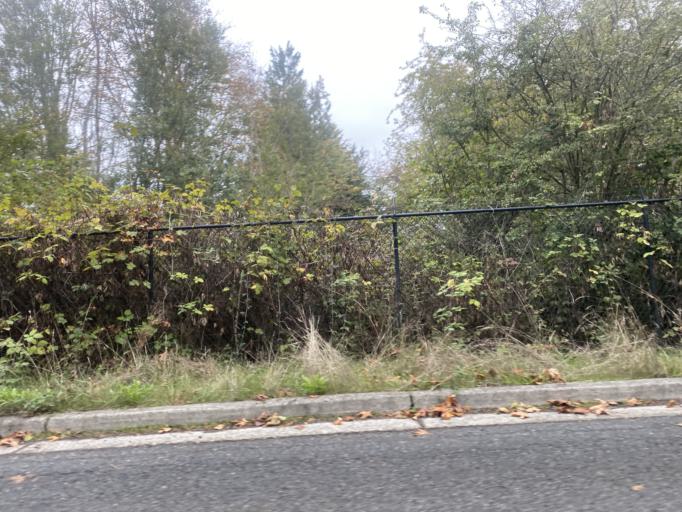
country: US
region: Washington
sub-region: King County
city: Seattle
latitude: 47.6644
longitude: -122.4087
